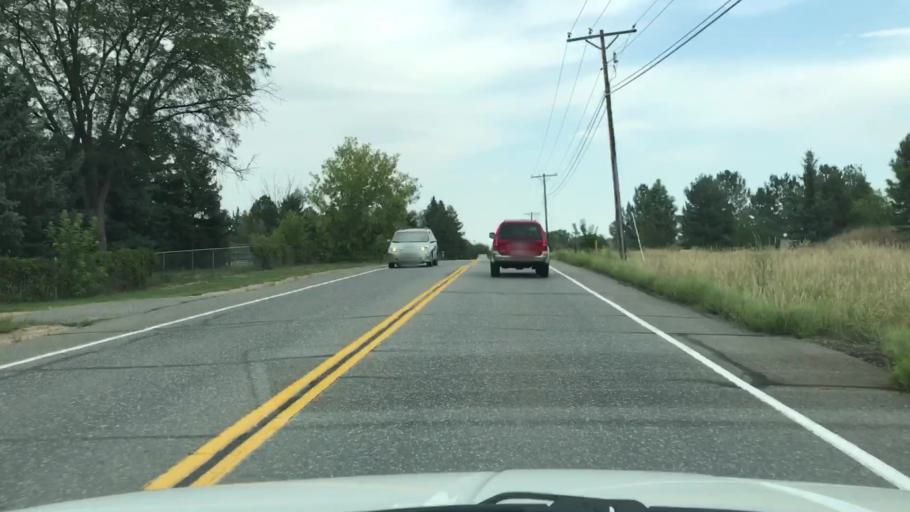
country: US
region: Colorado
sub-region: Boulder County
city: Louisville
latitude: 40.0001
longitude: -105.1455
